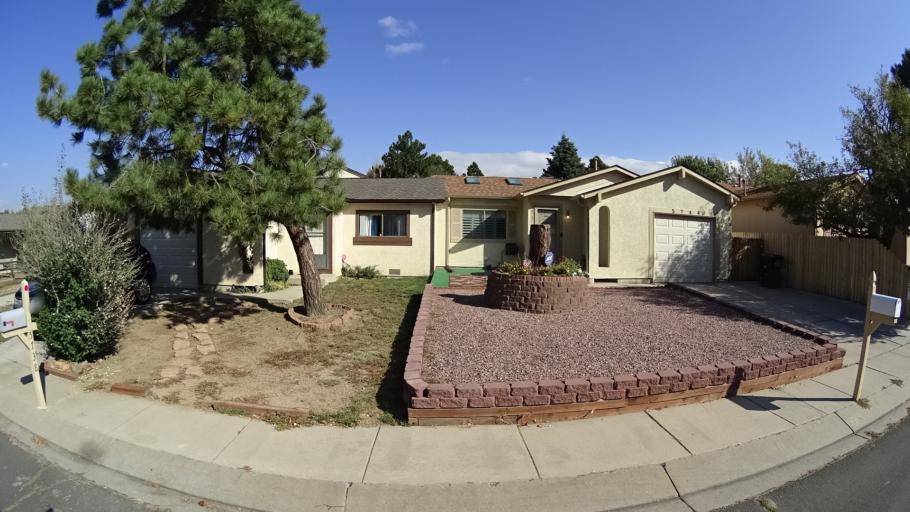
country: US
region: Colorado
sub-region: El Paso County
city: Cimarron Hills
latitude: 38.8810
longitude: -104.7214
